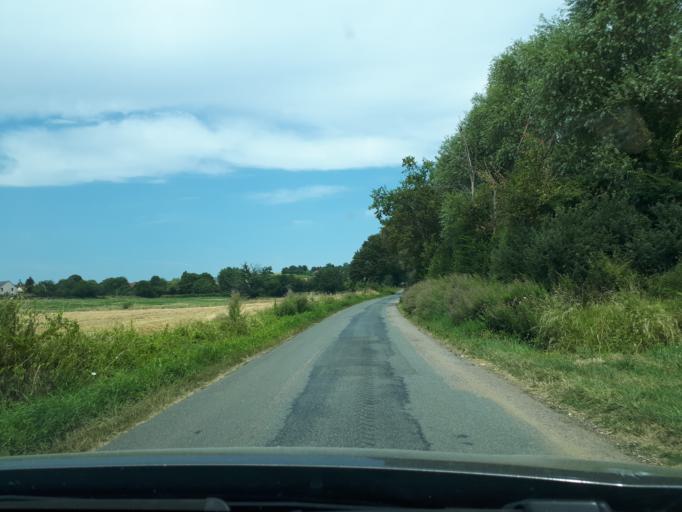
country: FR
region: Centre
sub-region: Departement du Cher
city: Sancerre
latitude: 47.3016
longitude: 2.7469
